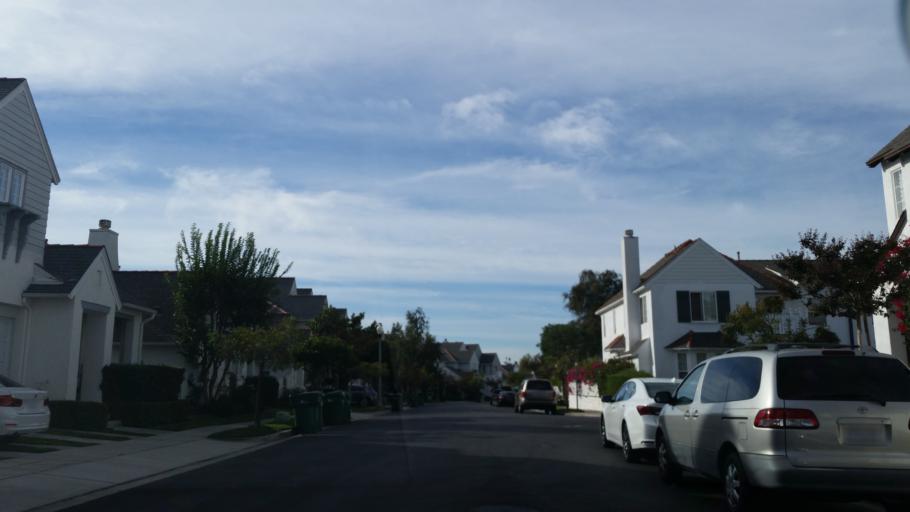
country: US
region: California
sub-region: Orange County
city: North Tustin
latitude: 33.7283
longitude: -117.7557
